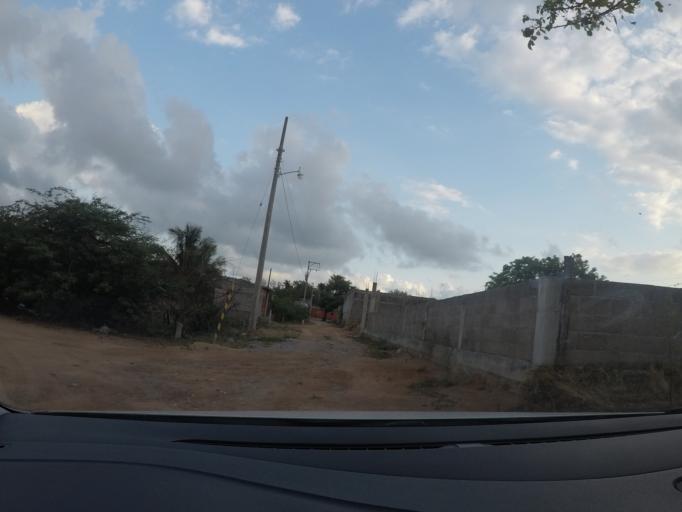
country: MX
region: Oaxaca
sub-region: Salina Cruz
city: Salina Cruz
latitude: 16.2060
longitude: -95.2020
